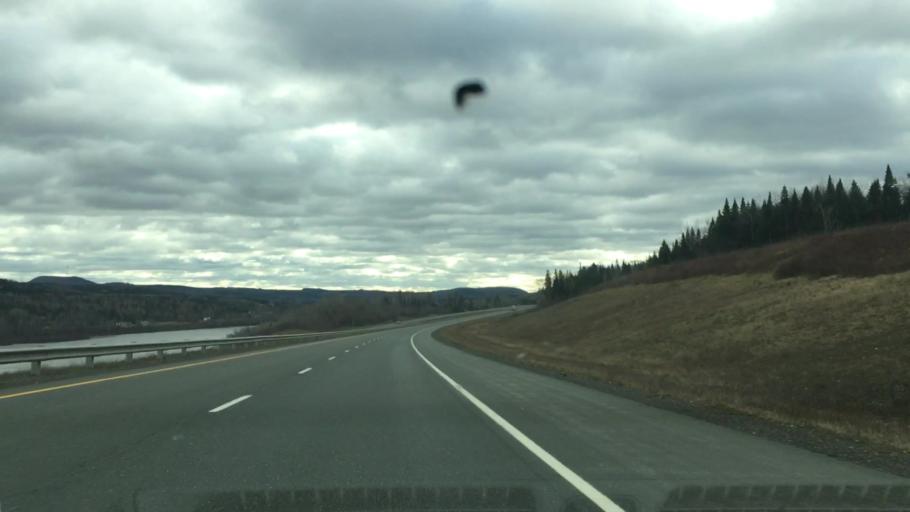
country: US
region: Maine
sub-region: Aroostook County
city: Fort Fairfield
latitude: 46.6797
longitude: -67.7310
